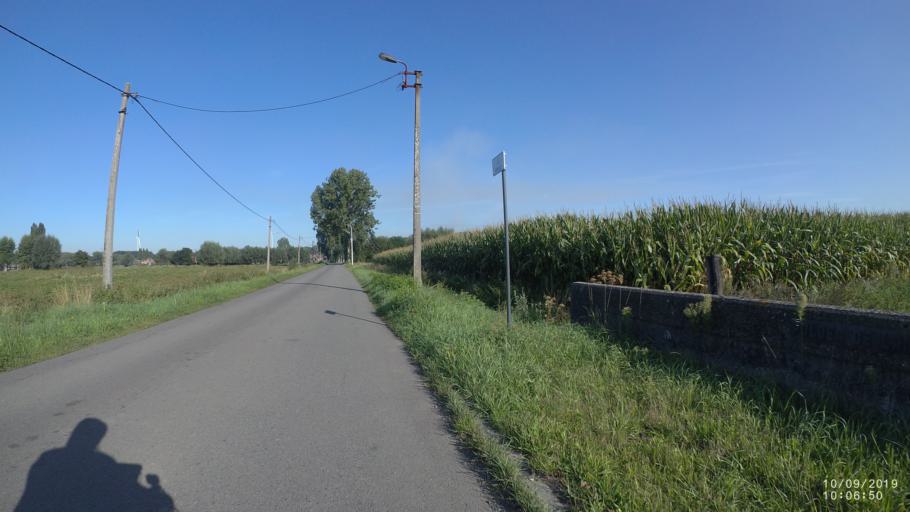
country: BE
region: Flanders
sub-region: Provincie Oost-Vlaanderen
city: Lochristi
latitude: 51.1419
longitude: 3.8226
